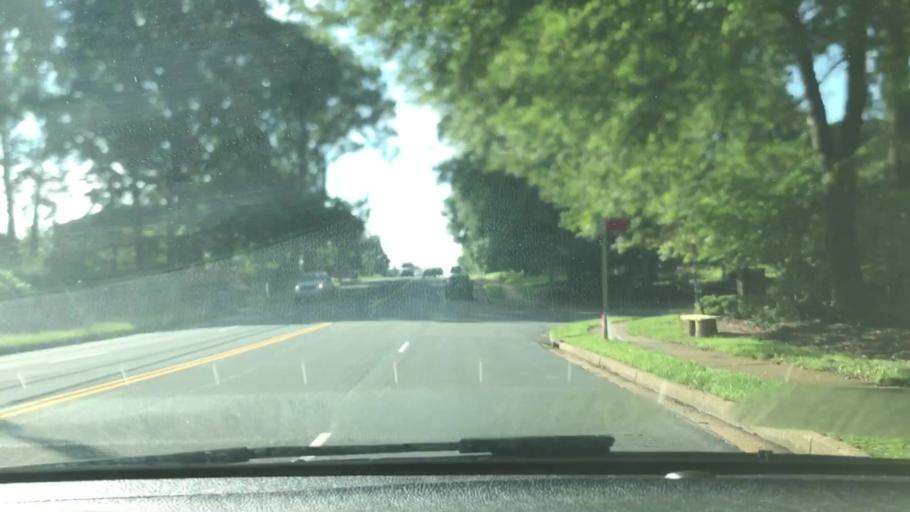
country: US
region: Virginia
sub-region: Fairfax County
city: Annandale
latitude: 38.8410
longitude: -77.1996
